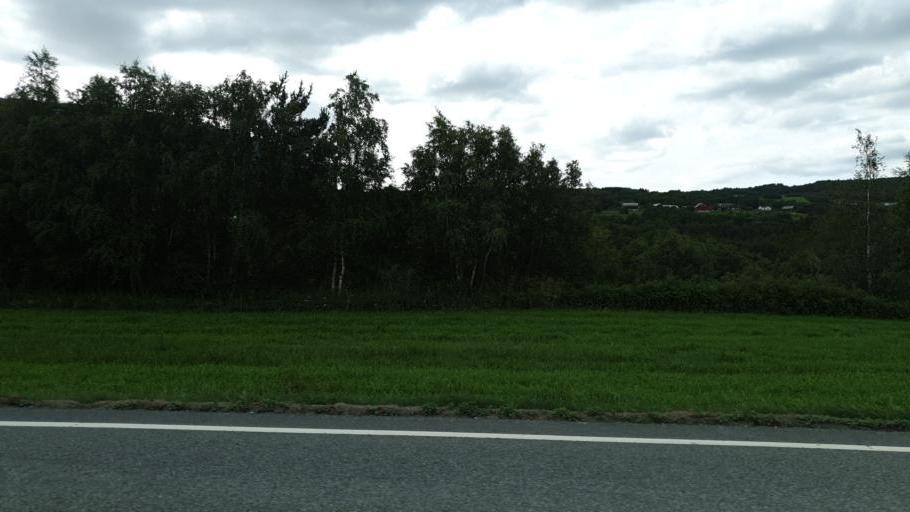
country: NO
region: Sor-Trondelag
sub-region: Oppdal
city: Oppdal
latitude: 62.5574
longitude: 9.6358
